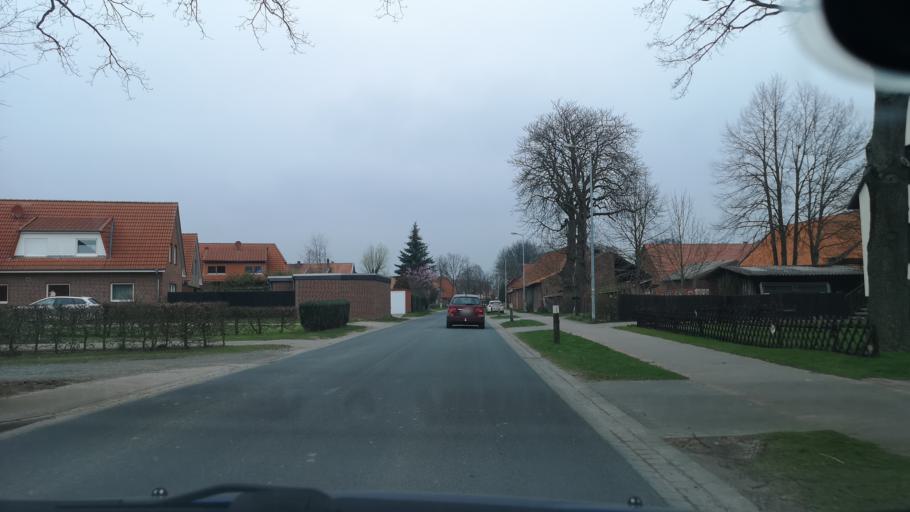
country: DE
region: Lower Saxony
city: Neustadt am Rubenberge
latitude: 52.5059
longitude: 9.5253
